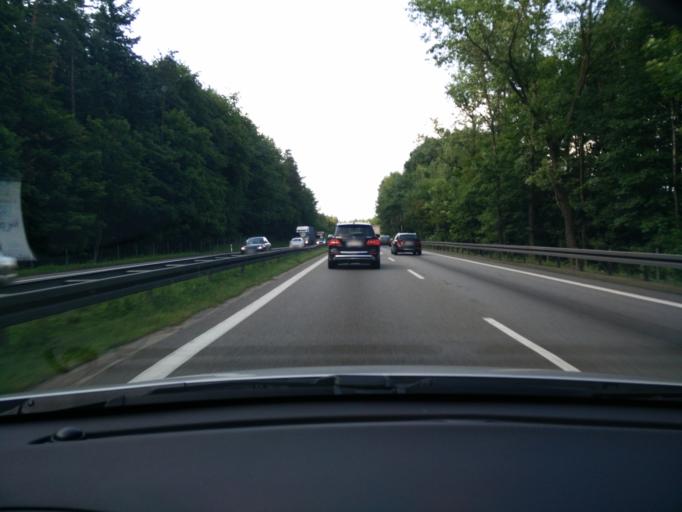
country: PL
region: Pomeranian Voivodeship
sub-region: Gdynia
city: Wielki Kack
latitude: 54.4411
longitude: 18.4896
